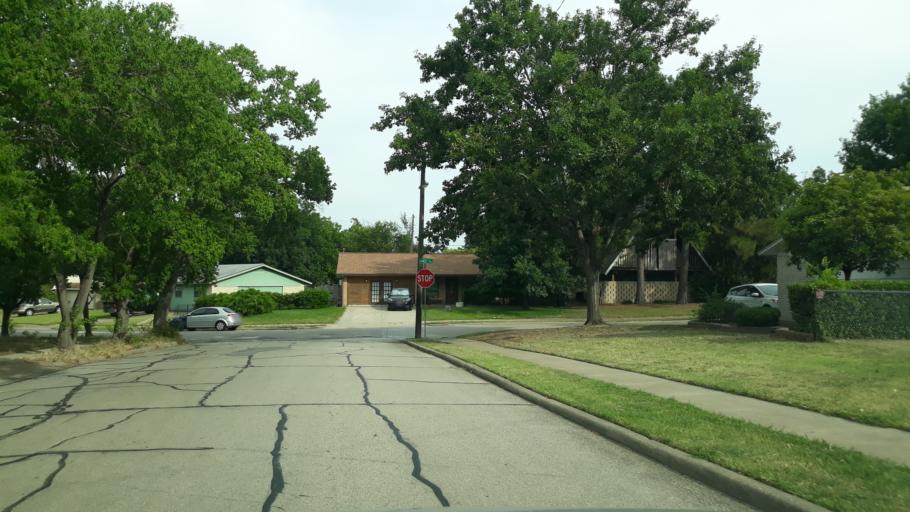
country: US
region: Texas
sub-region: Dallas County
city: Irving
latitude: 32.8439
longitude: -96.9886
